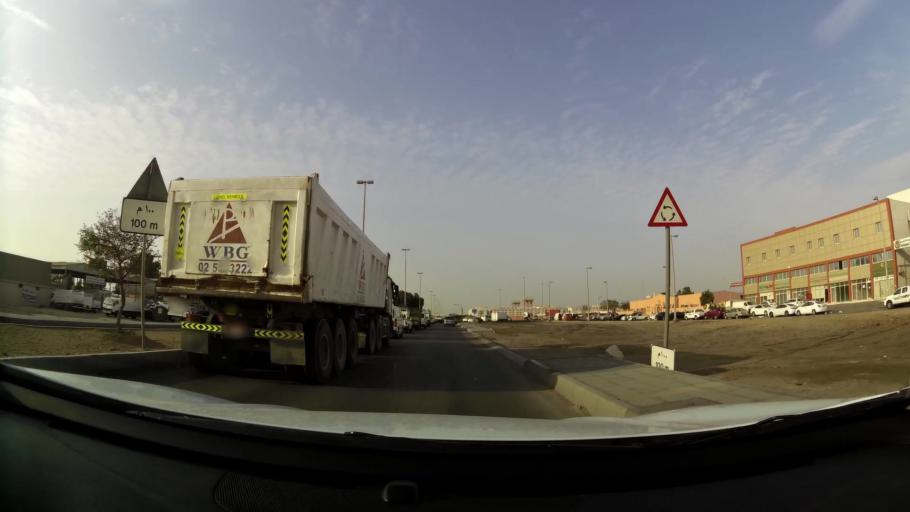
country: AE
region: Abu Dhabi
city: Abu Dhabi
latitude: 24.3539
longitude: 54.5170
